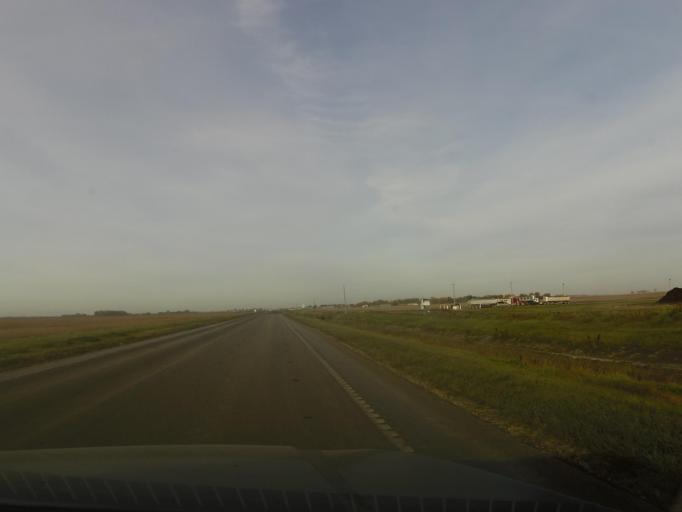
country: US
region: North Dakota
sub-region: Pembina County
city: Cavalier
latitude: 48.8045
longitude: -97.4303
